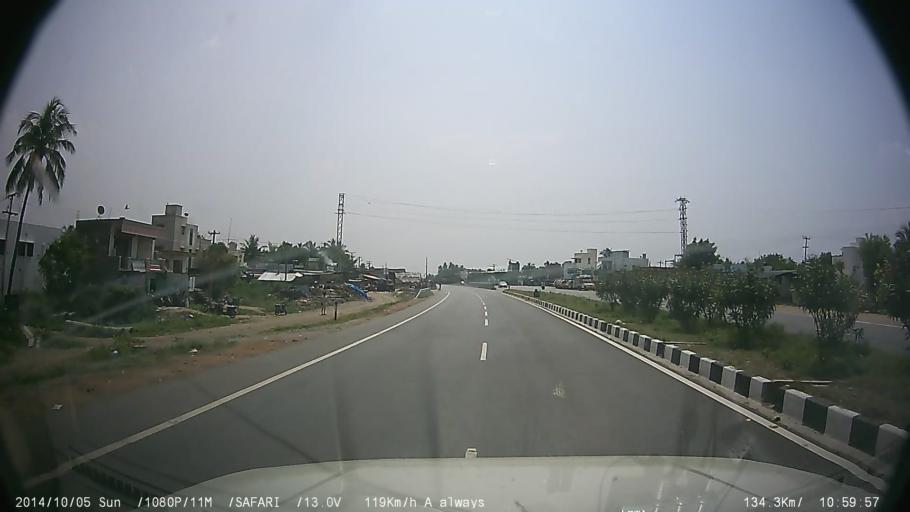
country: IN
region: Tamil Nadu
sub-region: Salem
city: Attur
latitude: 11.6282
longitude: 78.5378
